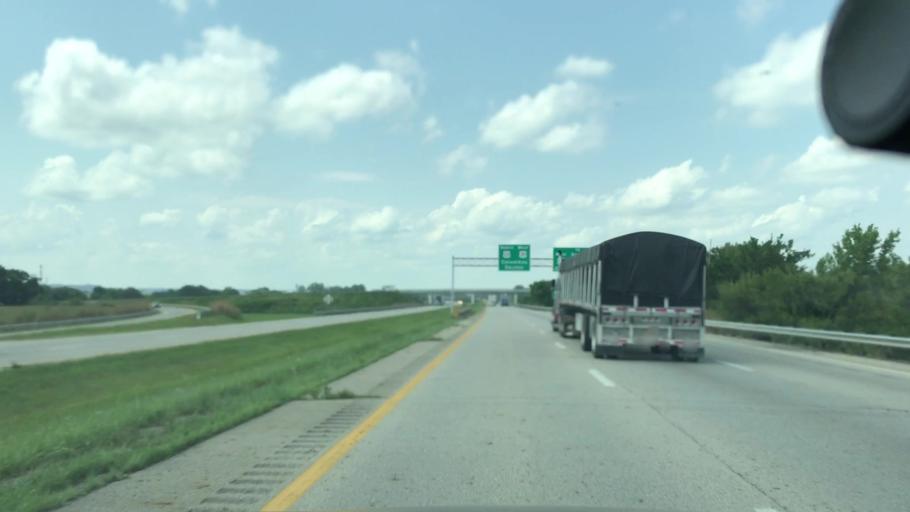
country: US
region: Ohio
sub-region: Ross County
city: Chillicothe
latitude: 39.3129
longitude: -82.9279
